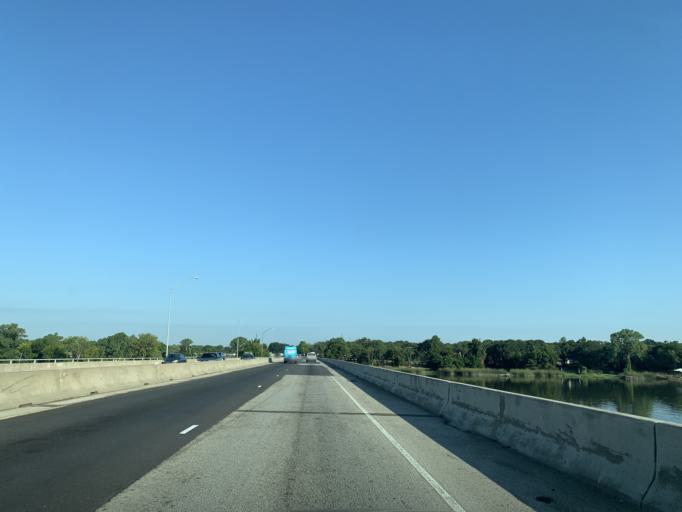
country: US
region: Texas
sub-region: Tarrant County
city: Lake Worth
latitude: 32.8203
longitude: -97.4453
